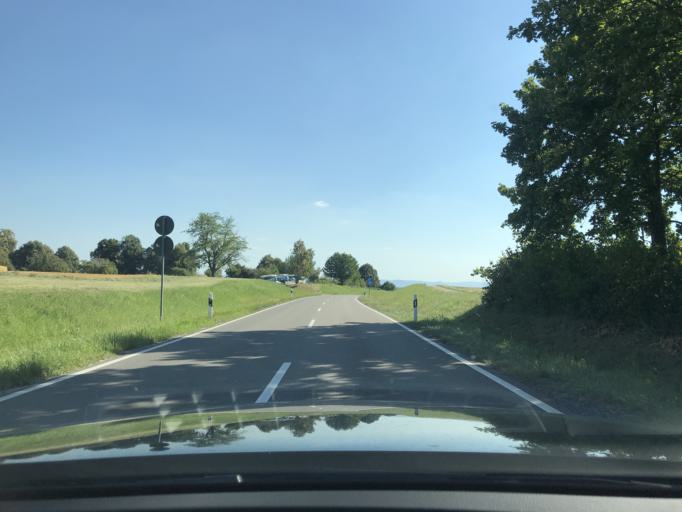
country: DE
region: Baden-Wuerttemberg
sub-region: Regierungsbezirk Stuttgart
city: Winterbach
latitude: 48.7585
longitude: 9.4896
